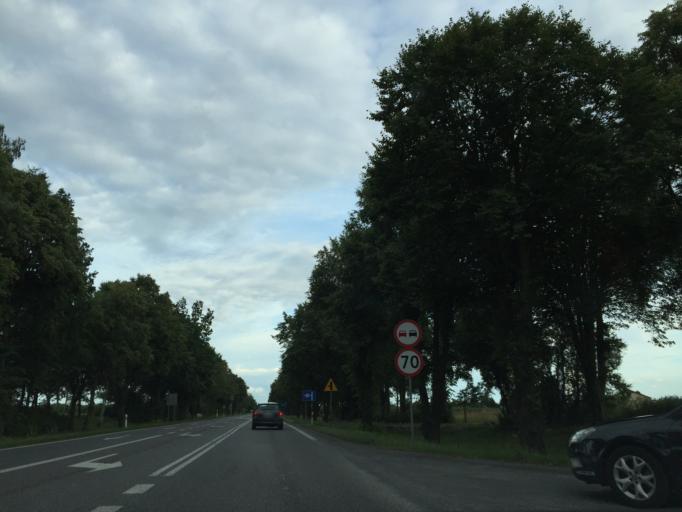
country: PL
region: Lublin Voivodeship
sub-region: Powiat lubartowski
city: Lubartow
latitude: 51.4922
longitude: 22.5766
